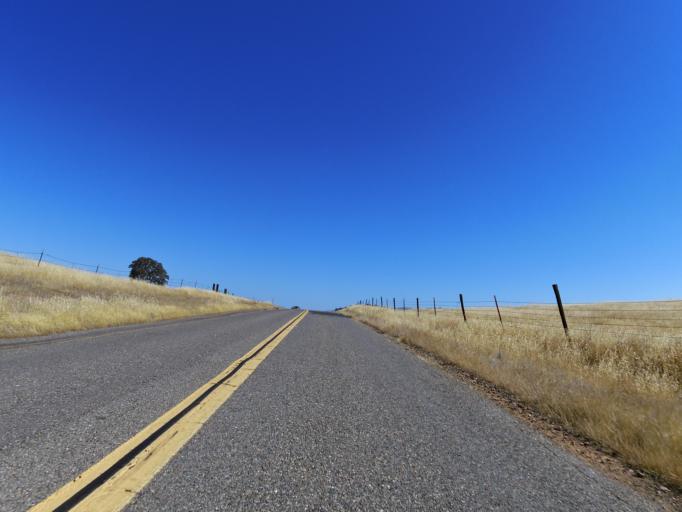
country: US
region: California
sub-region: Merced County
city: Planada
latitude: 37.5630
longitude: -120.3260
